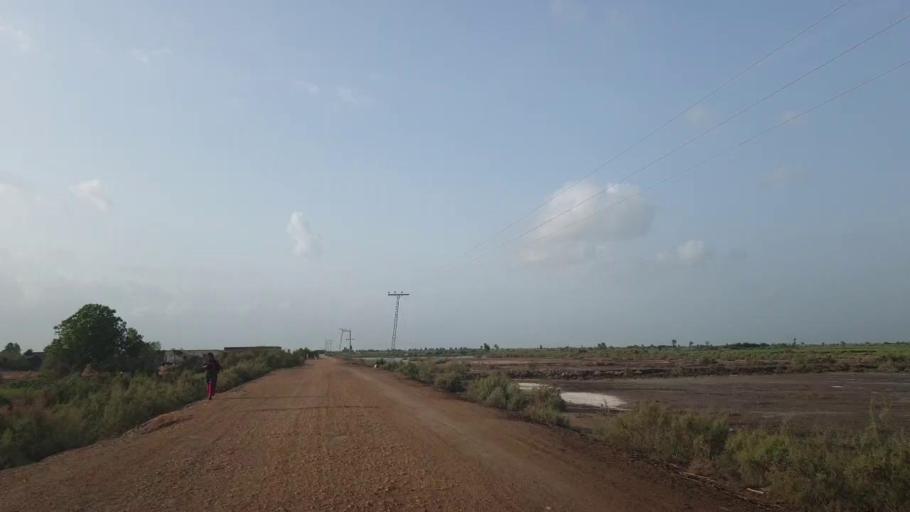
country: PK
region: Sindh
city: Tando Bago
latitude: 24.6502
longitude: 69.1119
